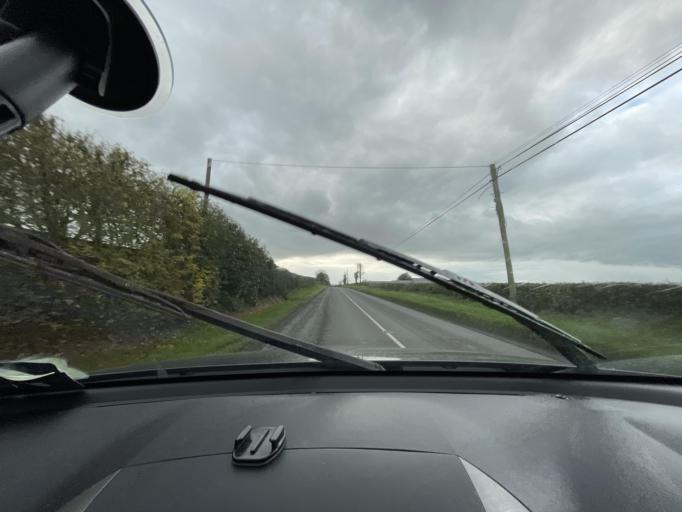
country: IE
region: Leinster
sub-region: Lu
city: Termonfeckin
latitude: 53.7480
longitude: -6.2900
